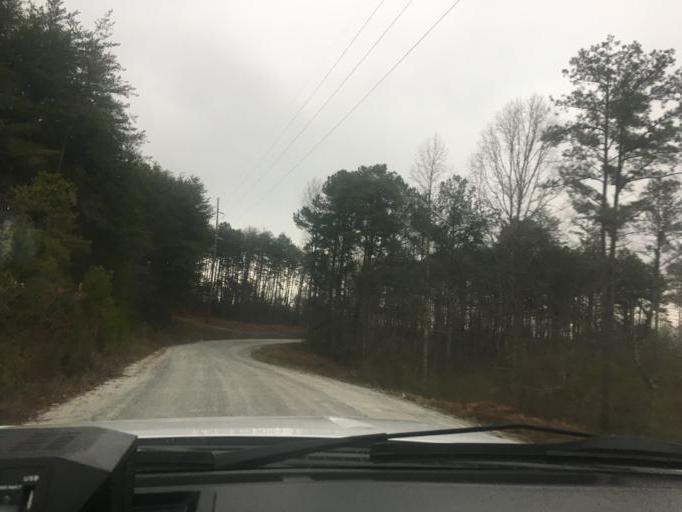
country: US
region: Georgia
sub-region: Dawson County
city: Dawsonville
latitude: 34.4414
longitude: -84.2210
